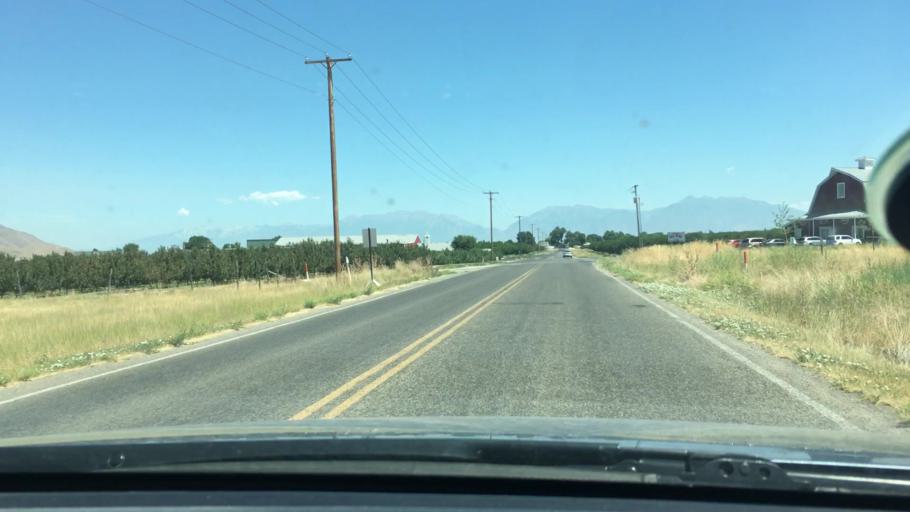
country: US
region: Utah
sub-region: Utah County
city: Santaquin
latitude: 39.9599
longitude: -111.7957
